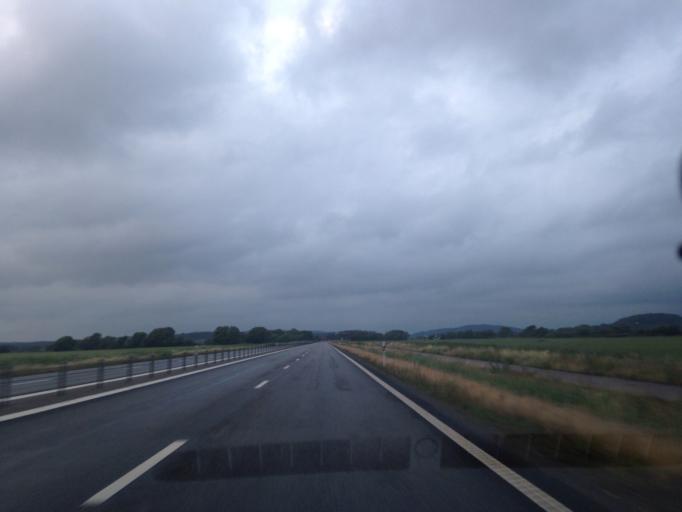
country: SE
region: Halland
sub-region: Varbergs Kommun
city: Varberg
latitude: 57.1339
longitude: 12.2627
